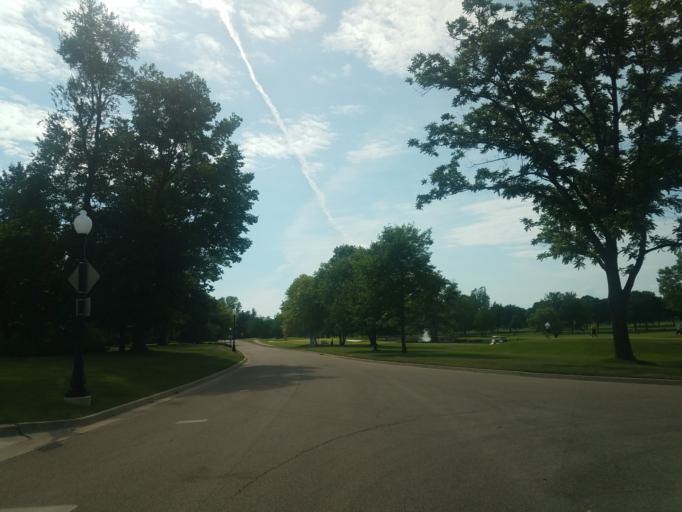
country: US
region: Illinois
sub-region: McLean County
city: Bloomington
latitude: 40.4820
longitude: -88.9640
